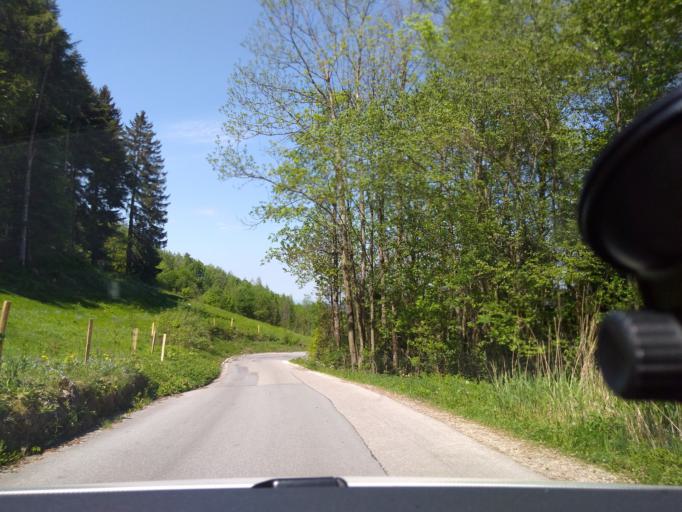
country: DE
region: Bavaria
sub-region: Upper Bavaria
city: Bernau am Chiemsee
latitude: 47.7939
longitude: 12.3602
